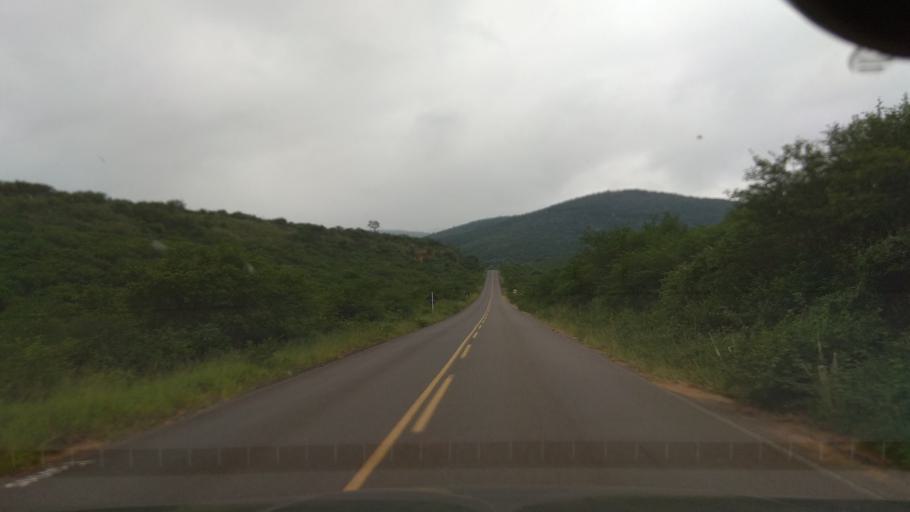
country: BR
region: Bahia
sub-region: Santa Ines
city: Santa Ines
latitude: -13.2519
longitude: -39.7773
